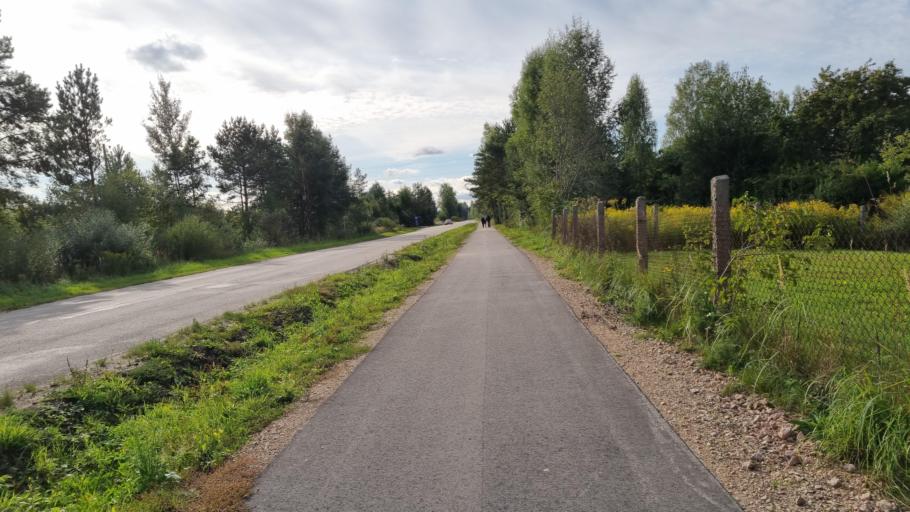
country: LV
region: Olaine
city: Olaine
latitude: 56.6994
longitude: 24.0720
